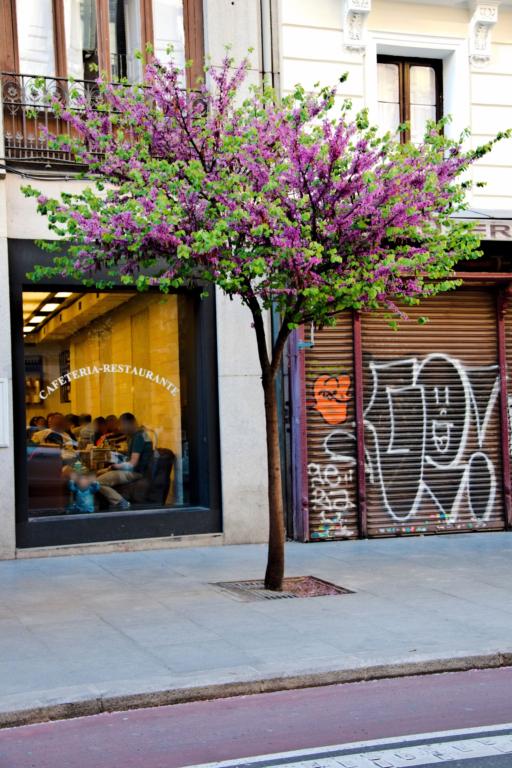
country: ES
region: Madrid
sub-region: Provincia de Madrid
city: Madrid
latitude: 40.4161
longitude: -3.7082
